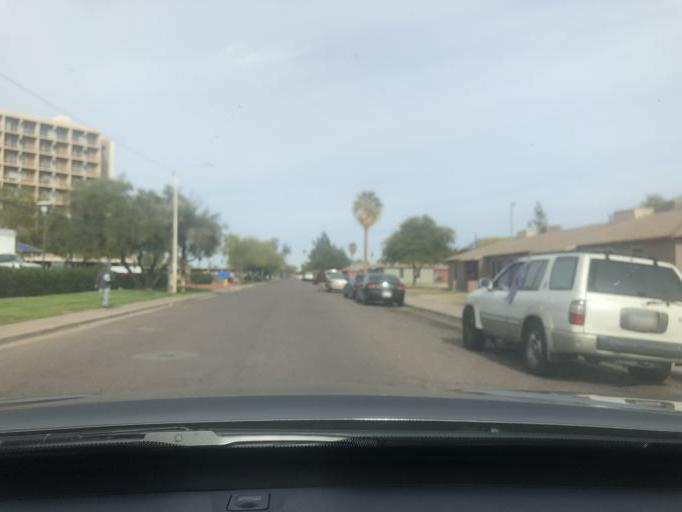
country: US
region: Arizona
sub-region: Maricopa County
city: Phoenix
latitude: 33.4534
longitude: -112.0412
